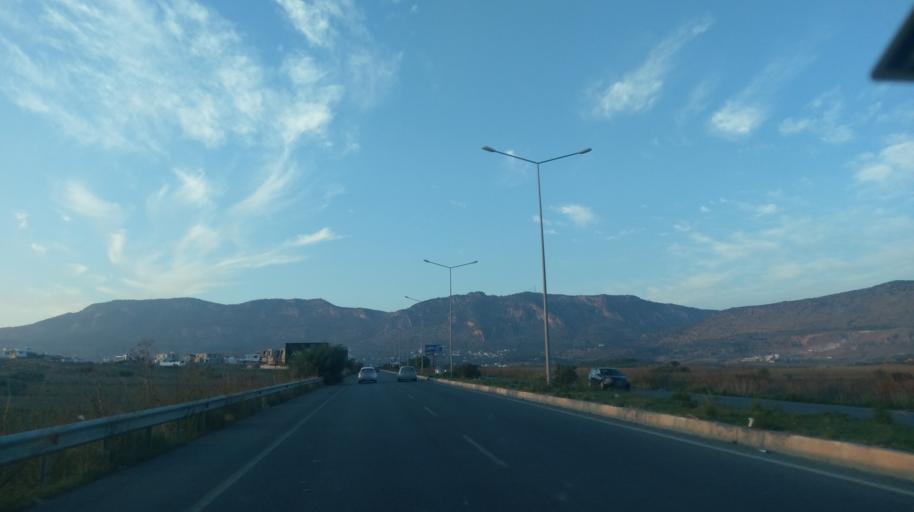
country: CY
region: Keryneia
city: Kyrenia
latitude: 35.2664
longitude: 33.2927
